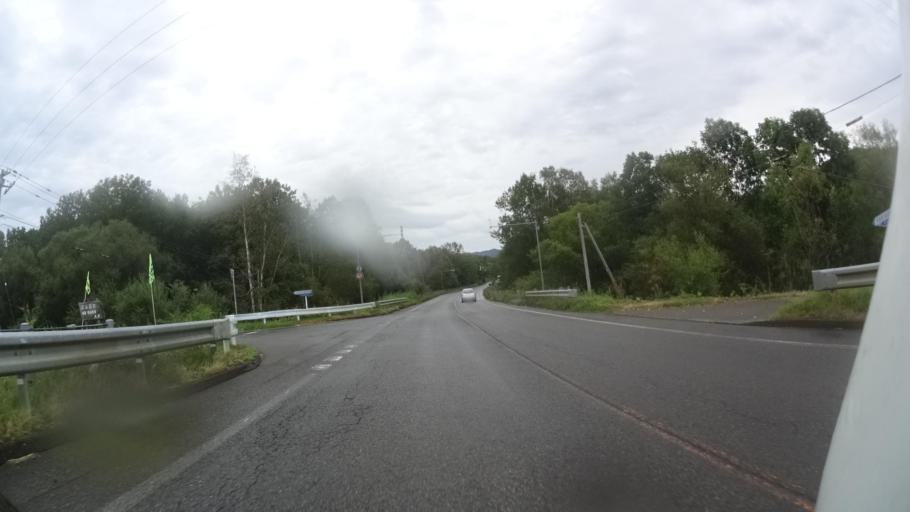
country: JP
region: Hokkaido
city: Kitami
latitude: 44.0925
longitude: 143.7519
